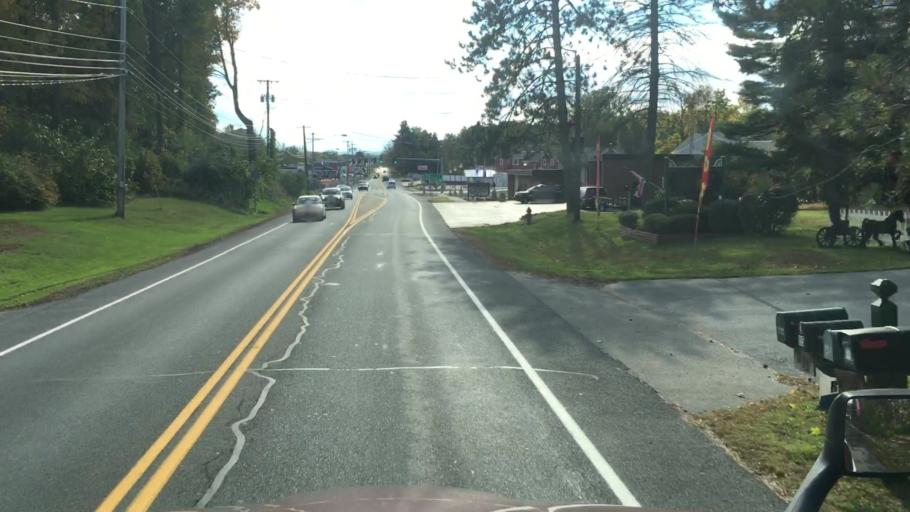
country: US
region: New York
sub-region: Schenectady County
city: East Glenville
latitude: 42.9117
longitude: -73.8973
